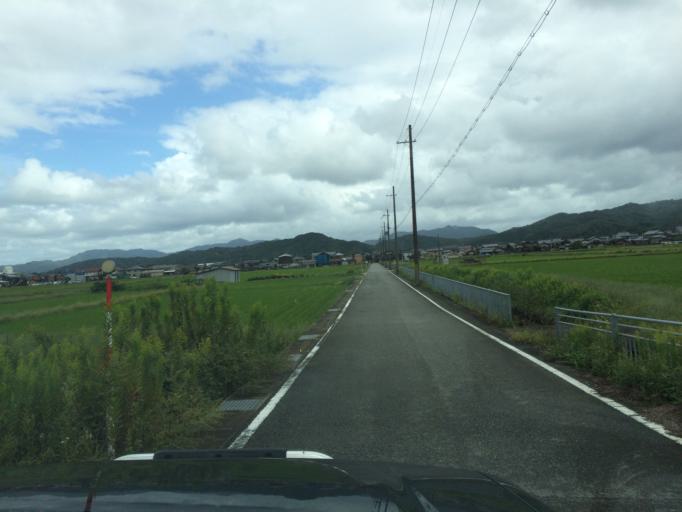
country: JP
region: Hyogo
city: Toyooka
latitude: 35.4871
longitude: 134.7935
